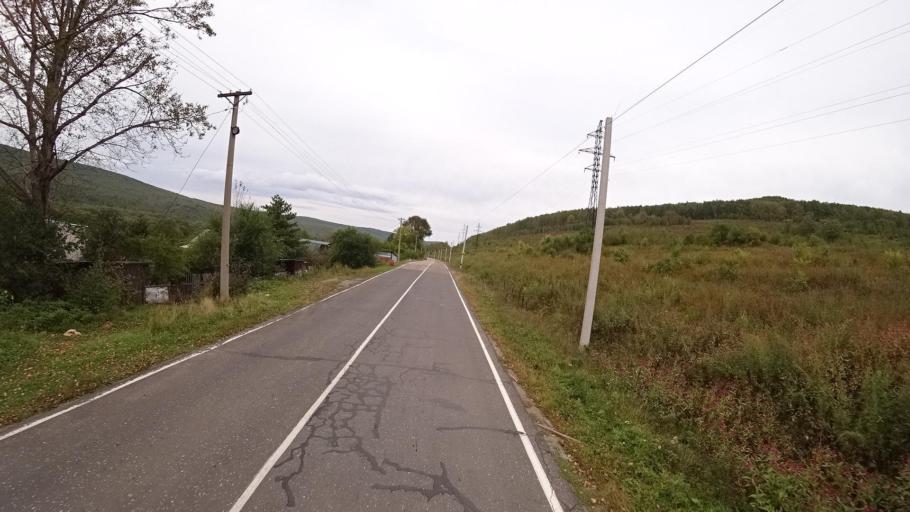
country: RU
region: Jewish Autonomous Oblast
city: Khingansk
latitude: 49.0393
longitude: 131.0590
